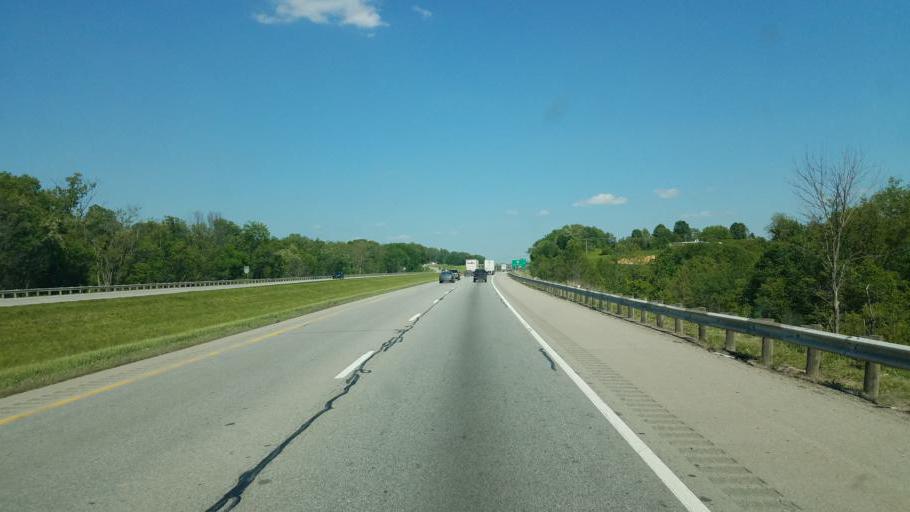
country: US
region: Ohio
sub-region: Muskingum County
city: Pleasant Grove
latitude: 39.9491
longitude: -81.9698
